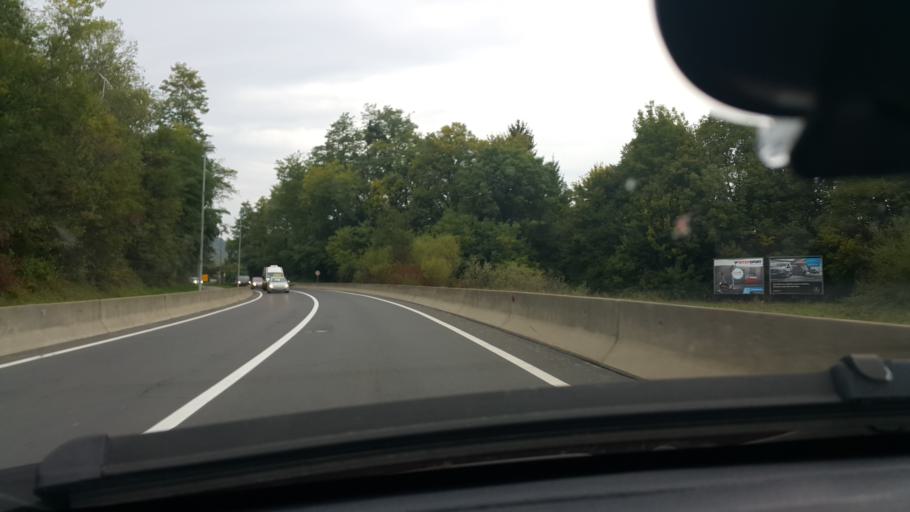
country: SI
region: Maribor
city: Kamnica
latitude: 46.5702
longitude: 15.6179
